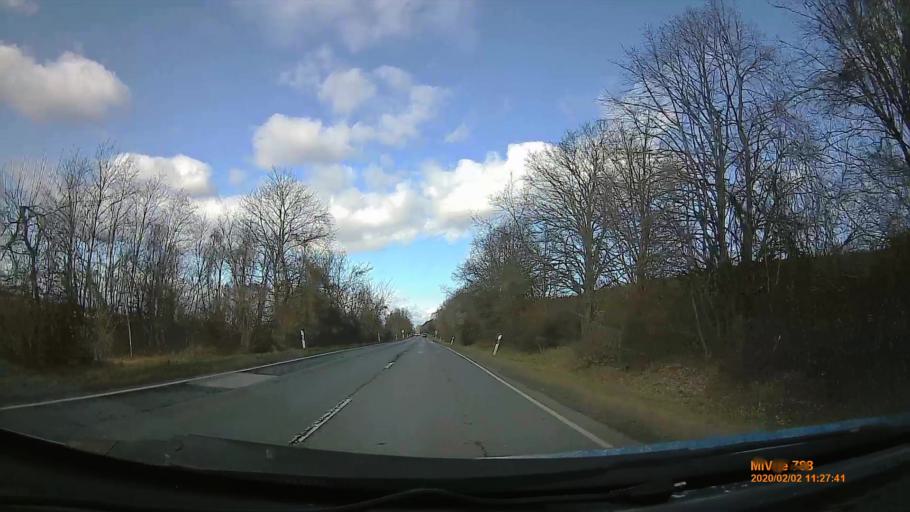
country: AT
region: Burgenland
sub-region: Eisenstadt-Umgebung
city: Klingenbach
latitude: 47.7202
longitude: 16.5663
